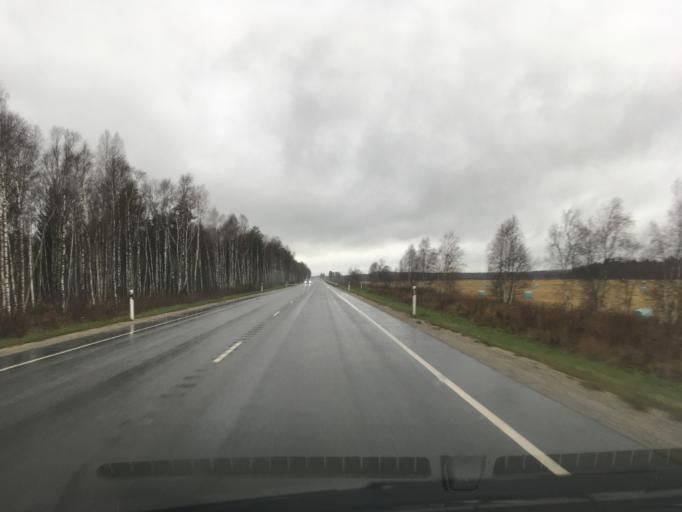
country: EE
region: Laeaene
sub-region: Lihula vald
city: Lihula
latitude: 58.7889
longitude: 24.0253
